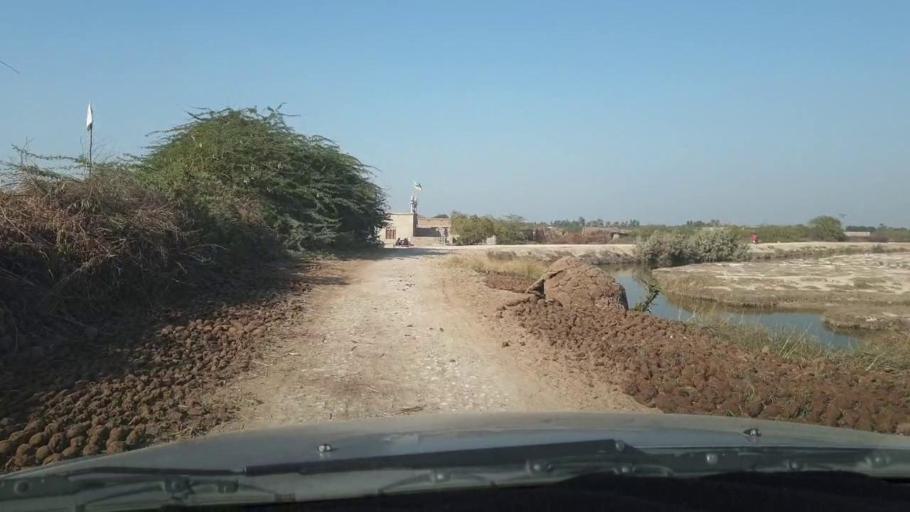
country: PK
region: Sindh
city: Mirpur Mathelo
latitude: 27.9744
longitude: 69.5602
